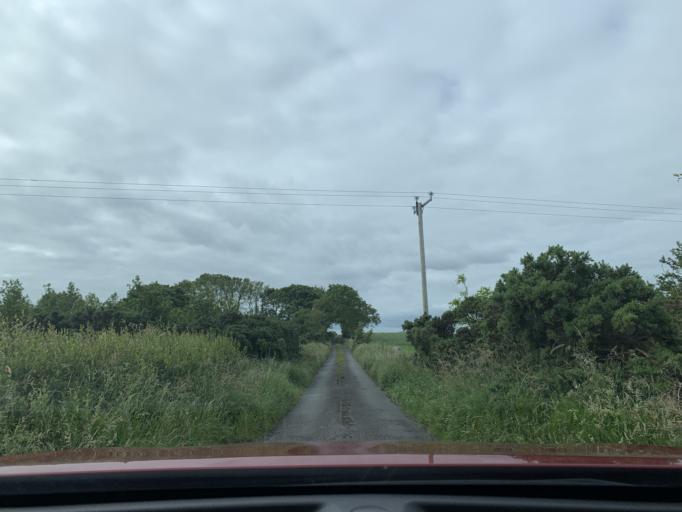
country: IE
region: Connaught
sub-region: Sligo
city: Sligo
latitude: 54.3670
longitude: -8.5206
